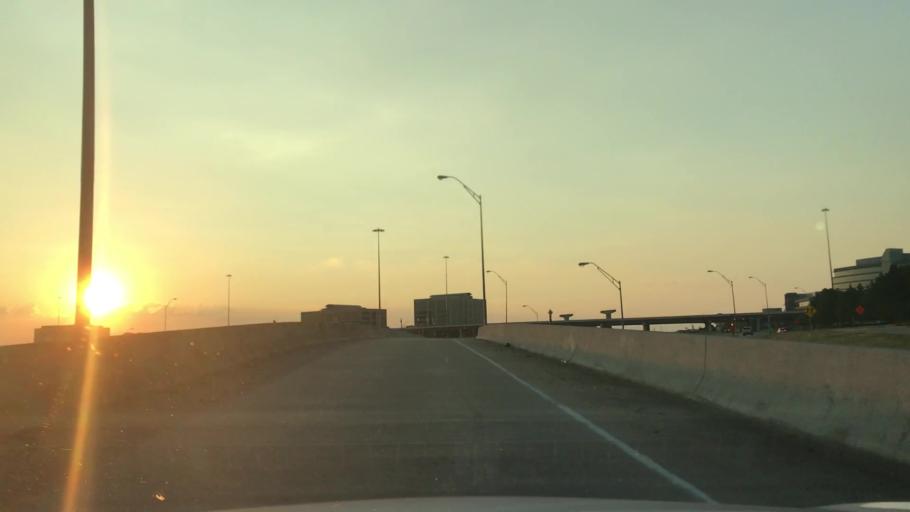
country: US
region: Texas
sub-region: Dallas County
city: Coppell
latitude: 32.8937
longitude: -96.9674
